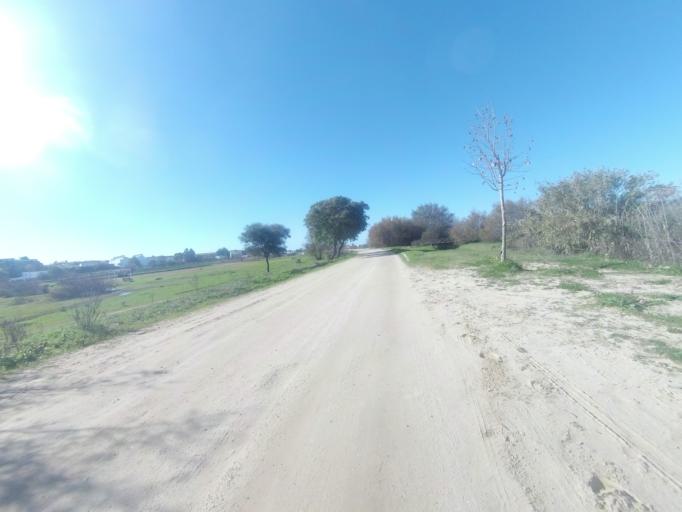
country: ES
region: Andalusia
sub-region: Provincia de Huelva
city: Palos de la Frontera
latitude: 37.2340
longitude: -6.8952
